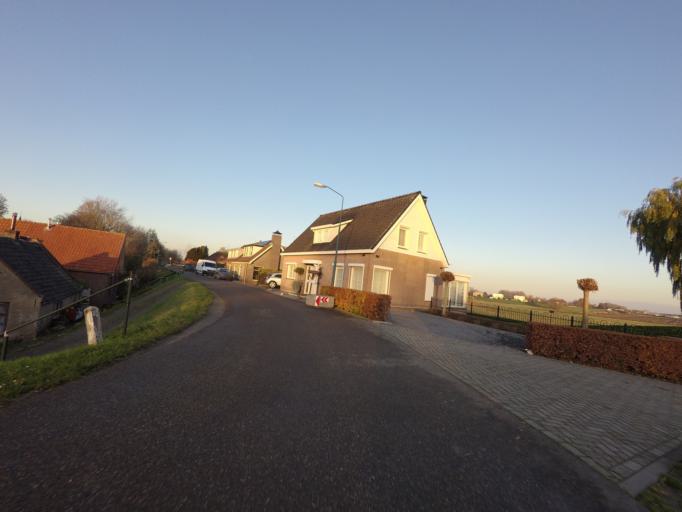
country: NL
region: Gelderland
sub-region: Gemeente Zaltbommel
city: Nederhemert-Noord
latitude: 51.7447
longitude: 5.2072
